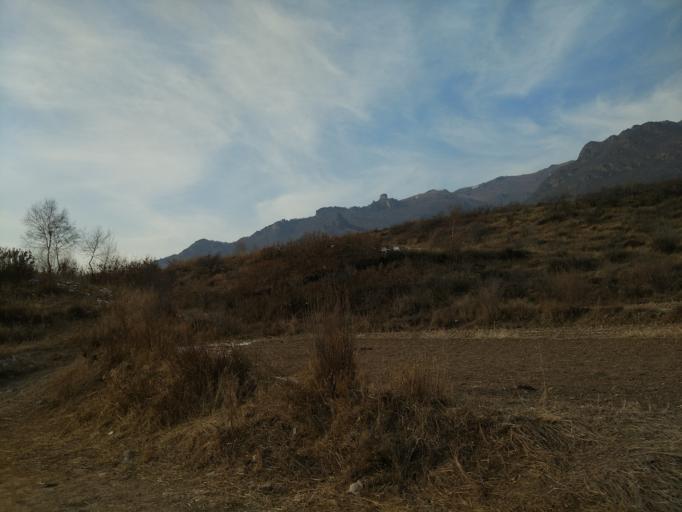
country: CN
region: Hebei
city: Xiwanzi
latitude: 40.8186
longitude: 115.4831
